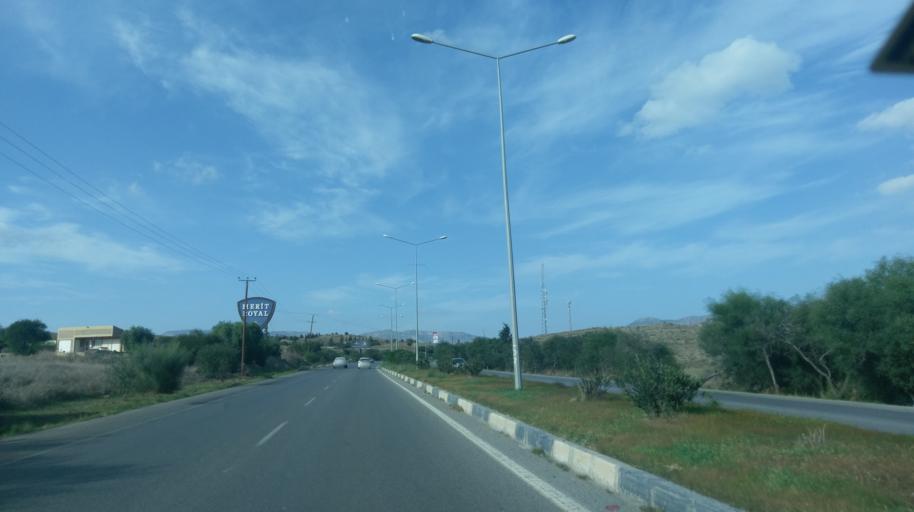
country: CY
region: Lefkosia
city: Nicosia
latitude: 35.2269
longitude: 33.3134
